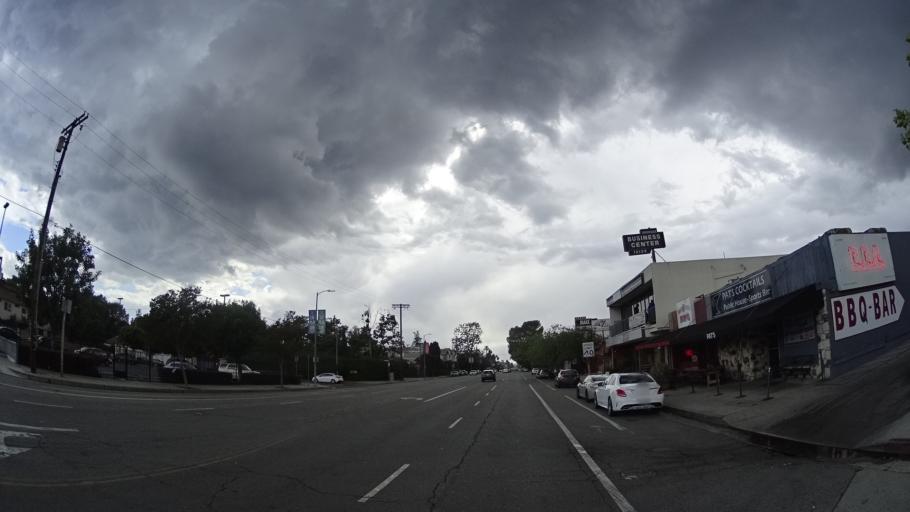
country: US
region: California
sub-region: Los Angeles County
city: North Hollywood
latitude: 34.1577
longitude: -118.3971
